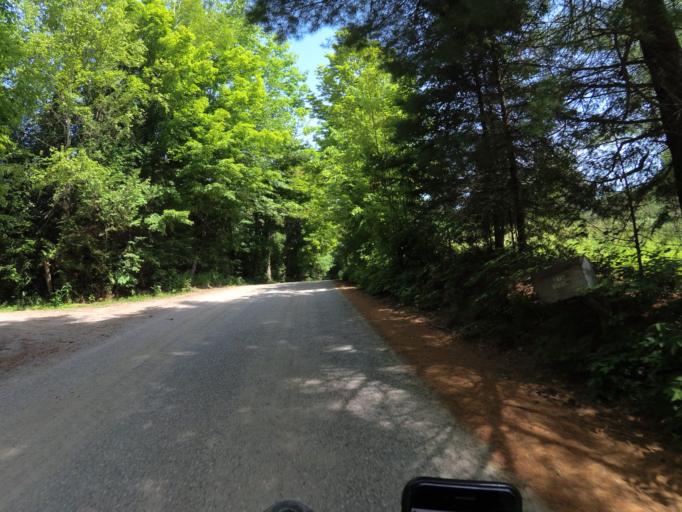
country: CA
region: Ontario
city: Skatepark
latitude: 44.7422
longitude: -76.8292
